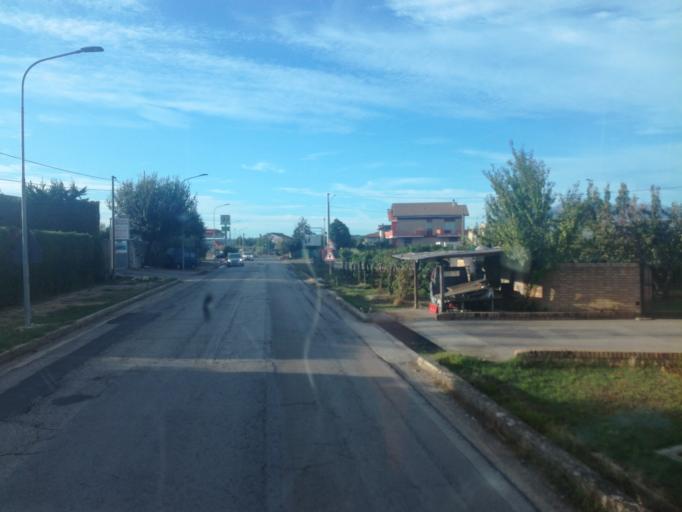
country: IT
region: Abruzzo
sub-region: Provincia di Chieti
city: Francavilla al Mare
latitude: 42.3925
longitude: 14.2964
